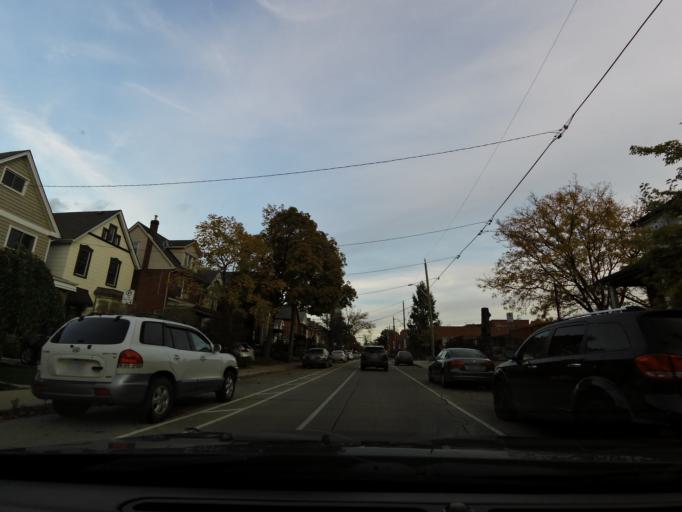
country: CA
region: Ontario
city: Hamilton
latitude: 43.2529
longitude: -79.8889
